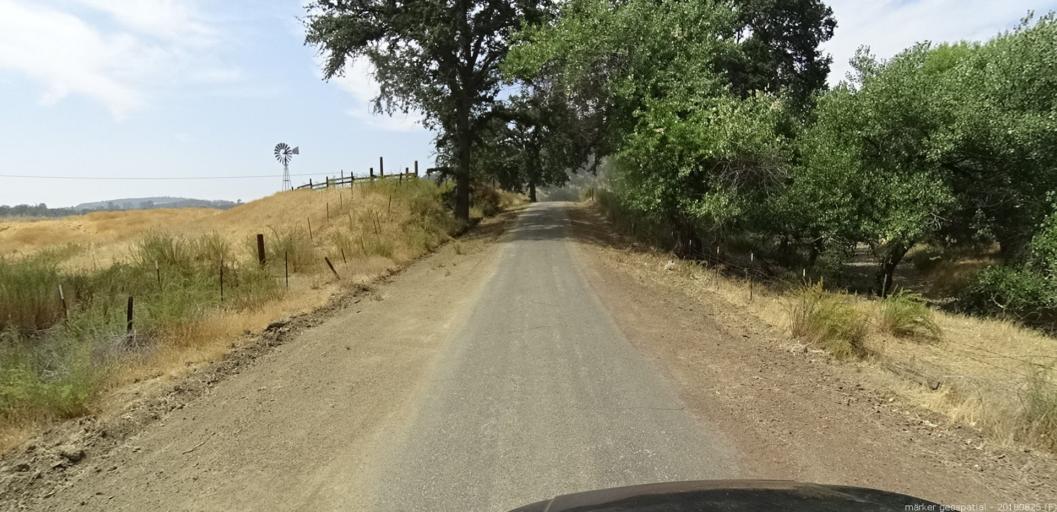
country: US
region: California
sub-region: Fresno County
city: Coalinga
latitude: 36.2136
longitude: -120.7052
